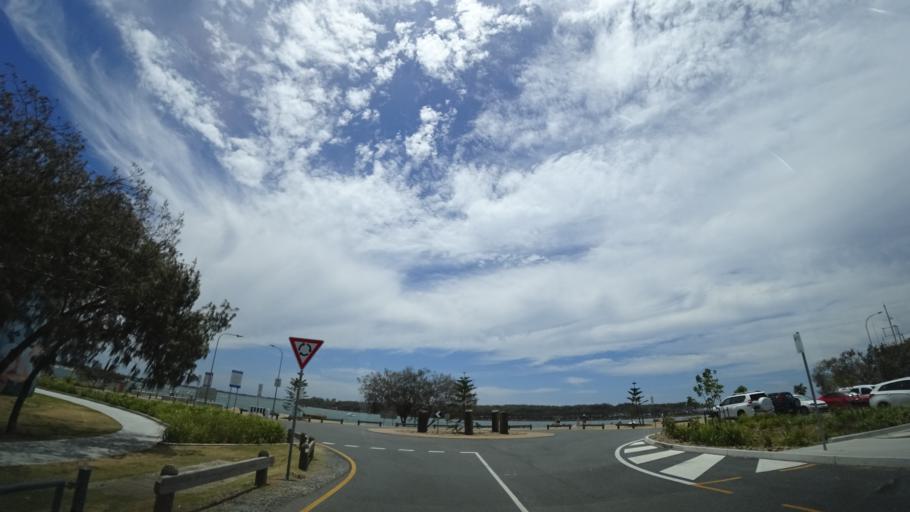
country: AU
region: Queensland
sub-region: Gold Coast
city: Southport
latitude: -27.9375
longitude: 153.4260
